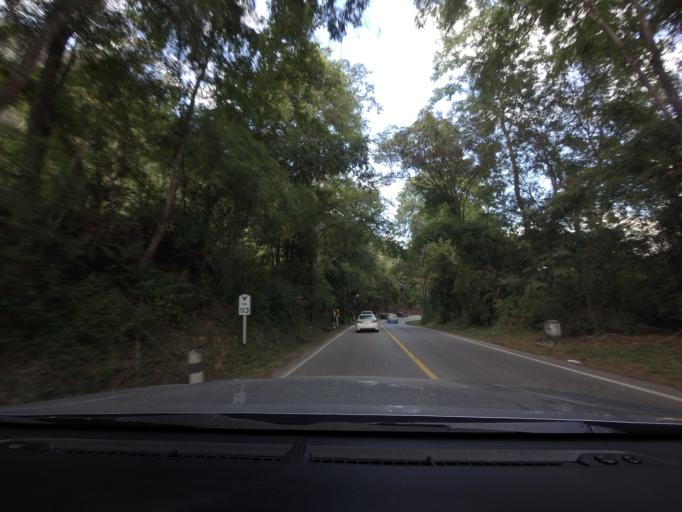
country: TH
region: Chiang Mai
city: Chai Prakan
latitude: 19.6060
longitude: 99.1222
